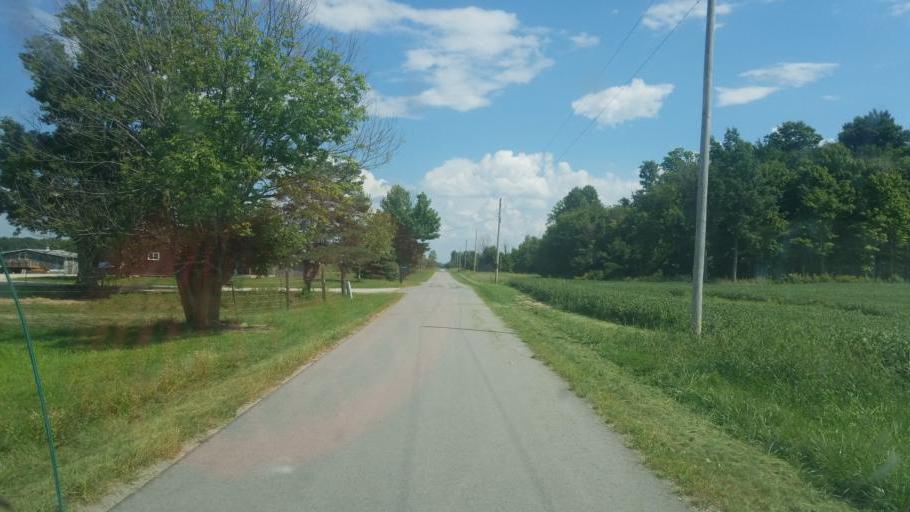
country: US
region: Ohio
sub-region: Wyandot County
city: Carey
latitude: 40.8754
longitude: -83.4163
